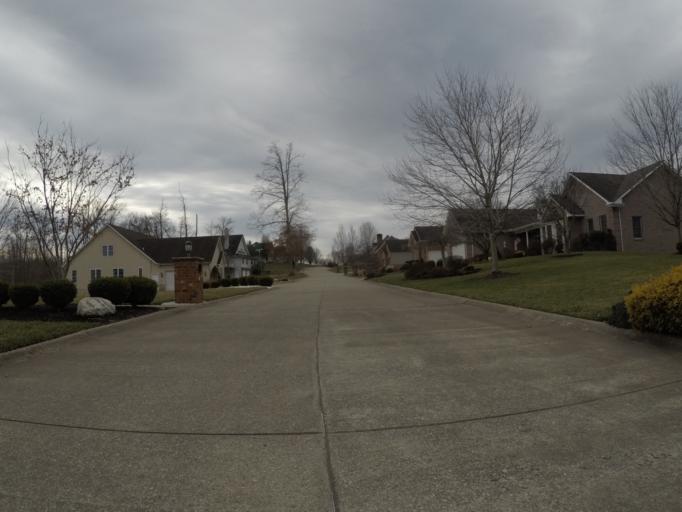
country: US
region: West Virginia
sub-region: Cabell County
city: Pea Ridge
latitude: 38.3977
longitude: -82.3774
